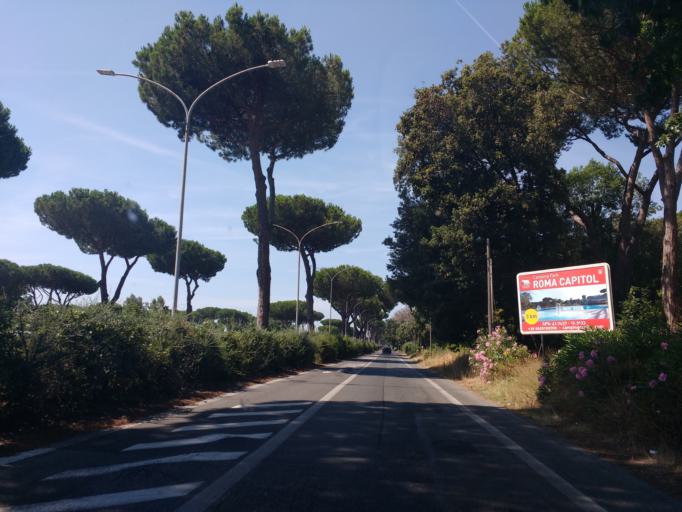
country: IT
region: Latium
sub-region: Citta metropolitana di Roma Capitale
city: Acilia-Castel Fusano-Ostia Antica
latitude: 41.7436
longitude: 12.3548
